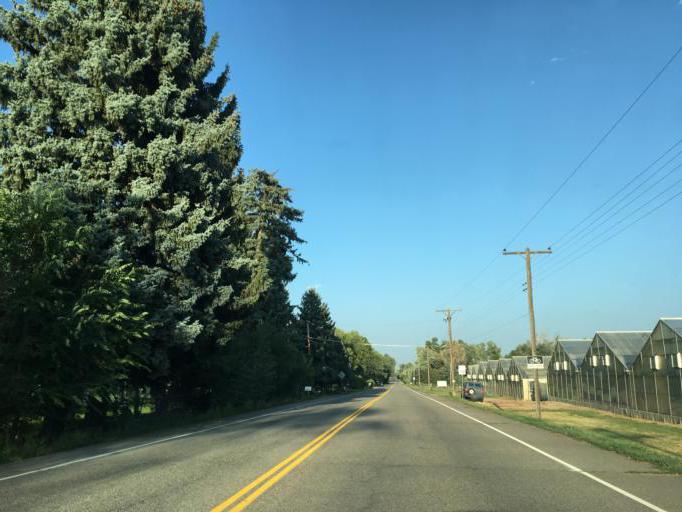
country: US
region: Colorado
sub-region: Jefferson County
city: Applewood
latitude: 39.7905
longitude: -105.1651
